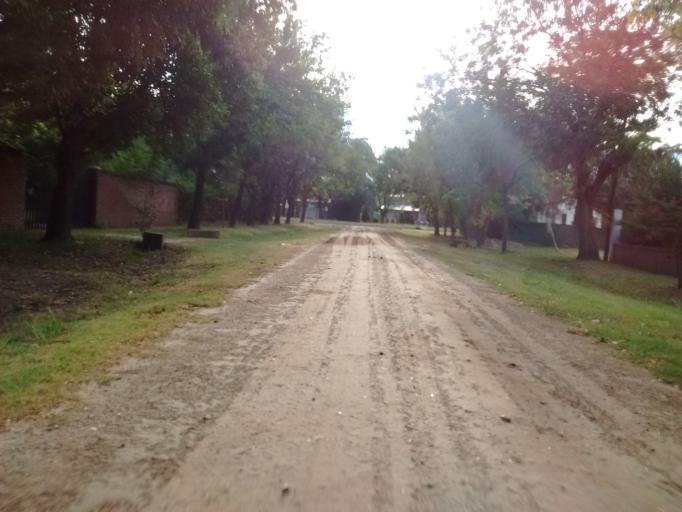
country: AR
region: Santa Fe
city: Funes
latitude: -32.9268
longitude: -60.8072
